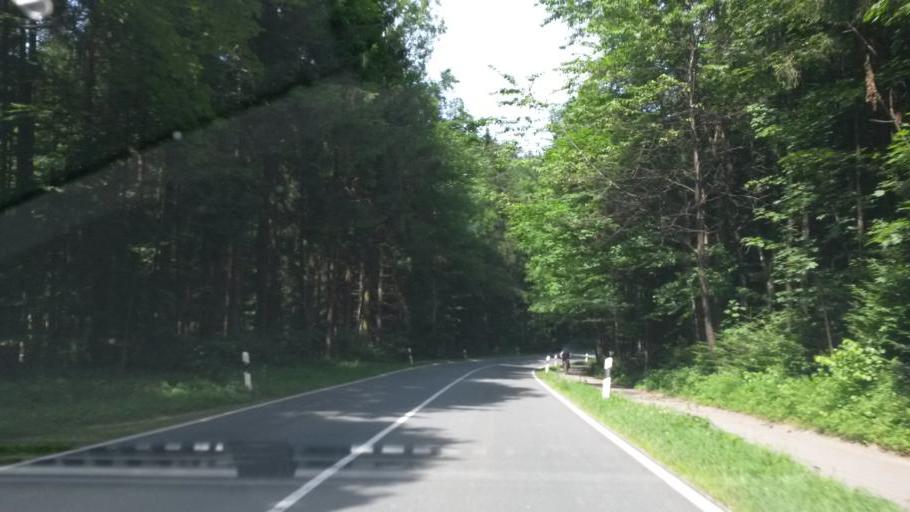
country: DE
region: Bavaria
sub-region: Upper Bavaria
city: Bernau am Chiemsee
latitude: 47.8010
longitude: 12.3535
